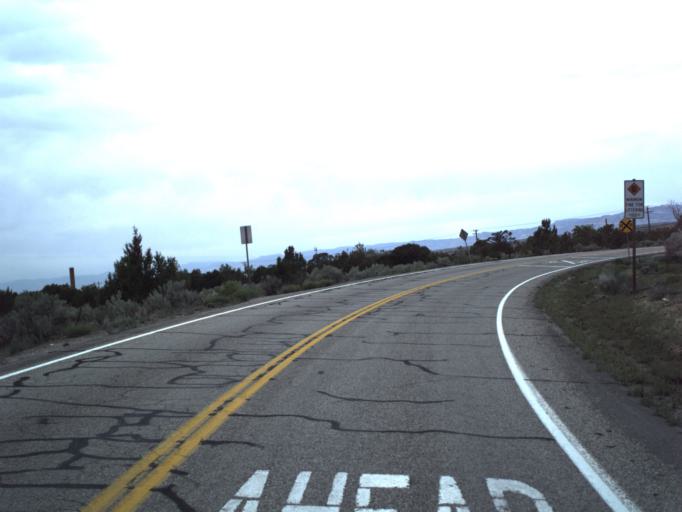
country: US
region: Utah
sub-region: Carbon County
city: East Carbon City
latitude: 39.5416
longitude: -110.4136
